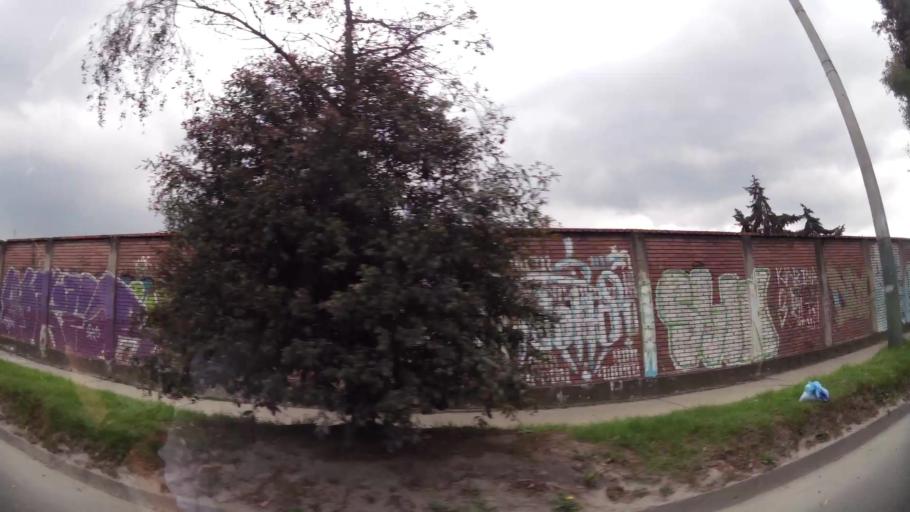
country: CO
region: Cundinamarca
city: La Calera
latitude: 4.7498
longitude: -74.0238
